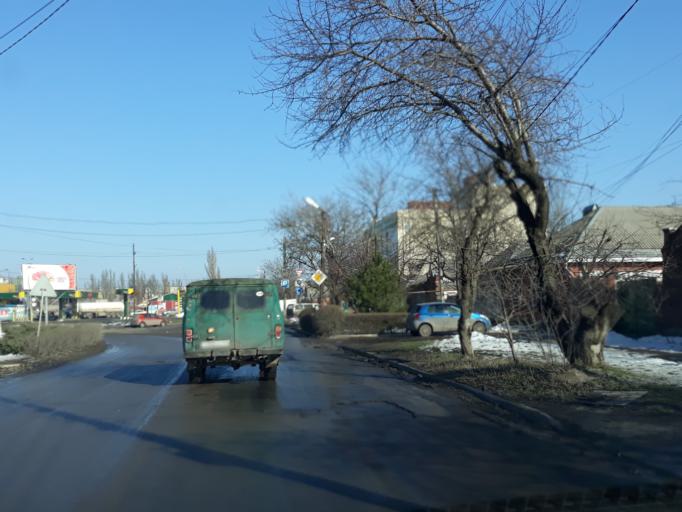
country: RU
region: Rostov
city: Taganrog
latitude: 47.2283
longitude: 38.8763
